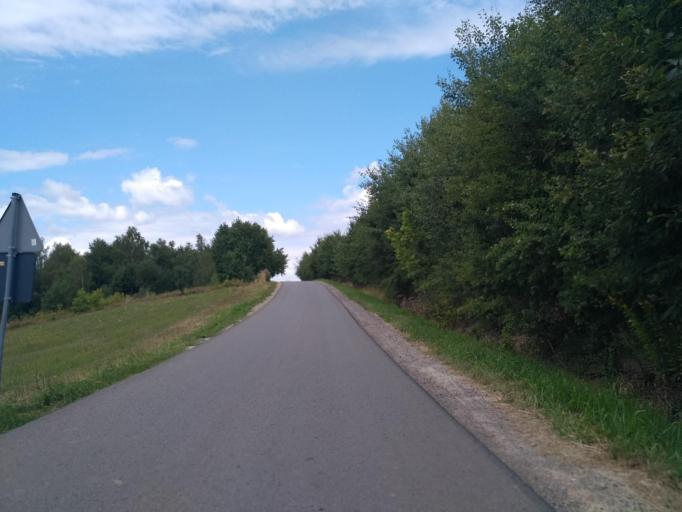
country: PL
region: Subcarpathian Voivodeship
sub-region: Powiat rzeszowski
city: Hyzne
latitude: 49.8999
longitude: 22.2295
